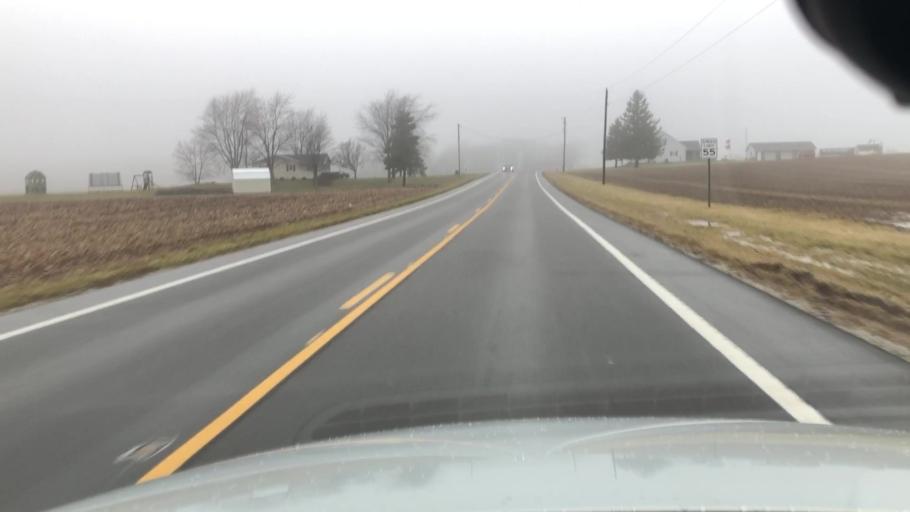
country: US
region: Ohio
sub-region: Logan County
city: Lakeview
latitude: 40.6055
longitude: -83.8855
